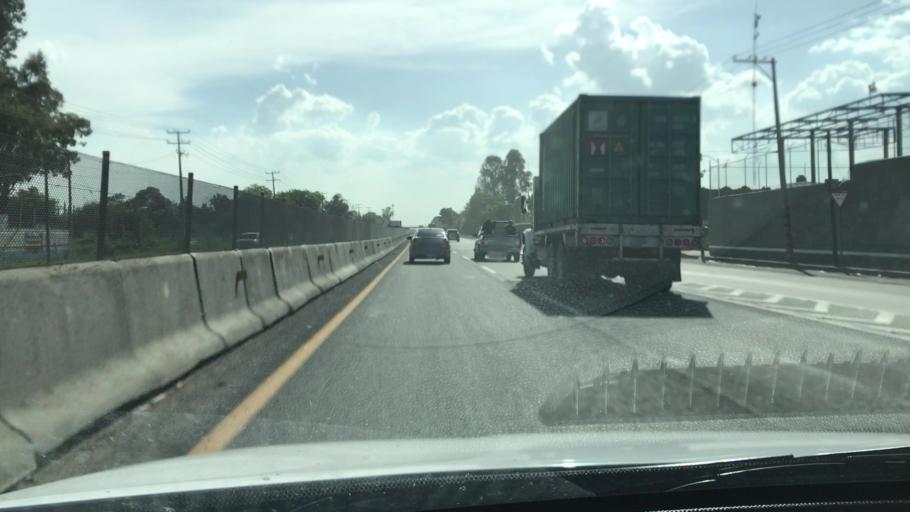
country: MX
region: Guanajuato
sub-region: Cortazar
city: Colonia la Calzada (La Olla)
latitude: 20.5108
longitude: -100.9594
